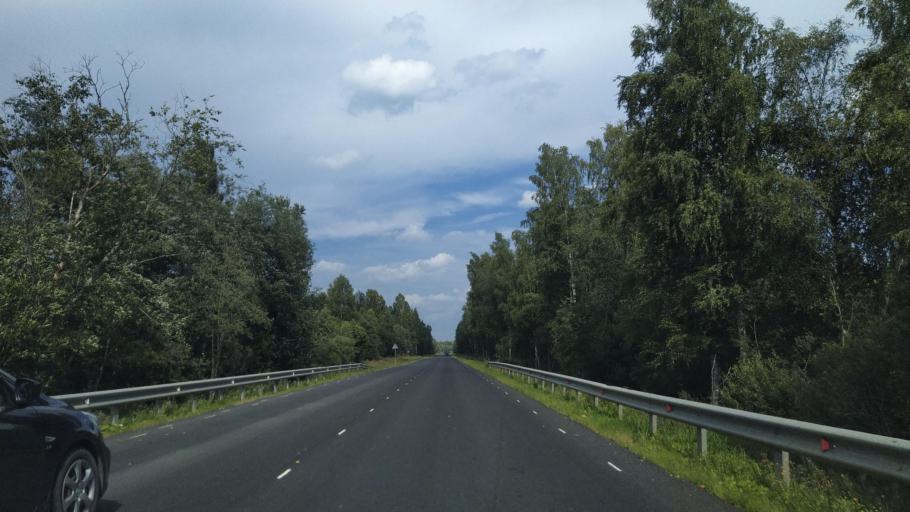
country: RU
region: Pskov
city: Vybor
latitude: 57.7200
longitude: 28.9494
